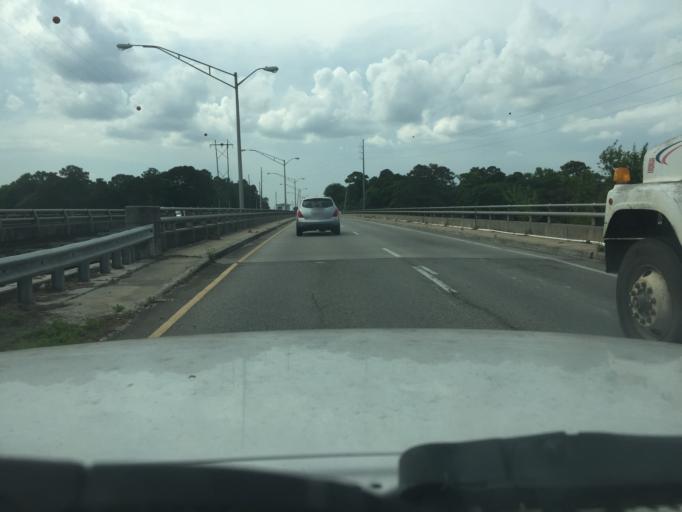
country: US
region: Georgia
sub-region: Chatham County
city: Whitemarsh Island
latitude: 32.0614
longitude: -81.0281
